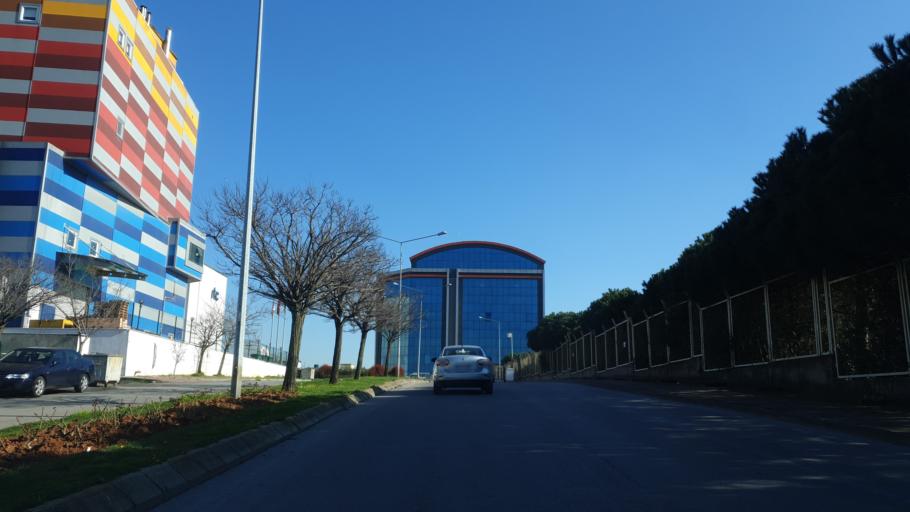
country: TR
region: Kocaeli
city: Balcik
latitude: 40.8764
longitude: 29.3723
